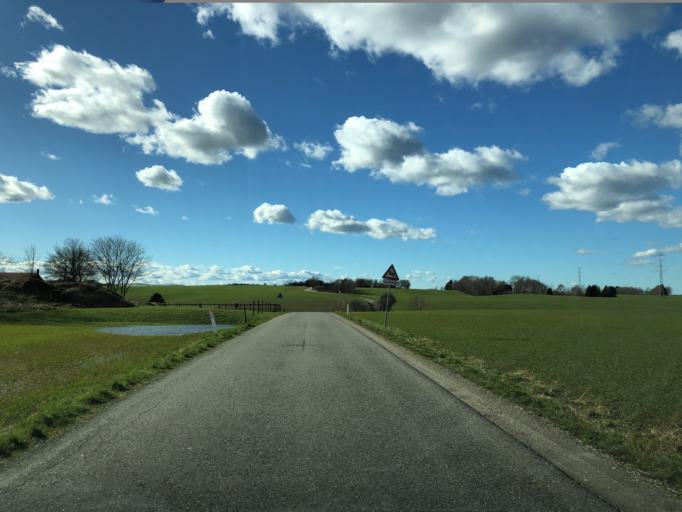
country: DK
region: Central Jutland
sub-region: Favrskov Kommune
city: Hadsten
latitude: 56.2911
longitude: 9.9803
